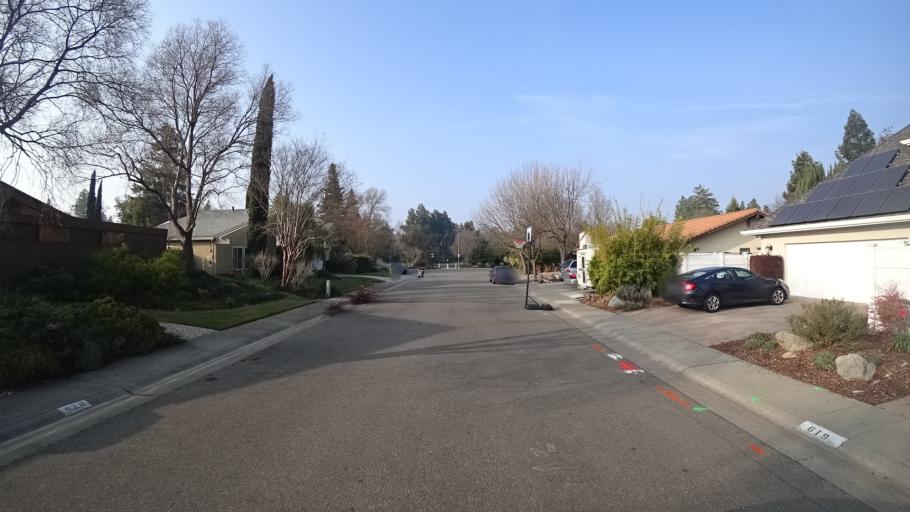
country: US
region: California
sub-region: Yolo County
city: Davis
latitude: 38.5651
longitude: -121.7551
